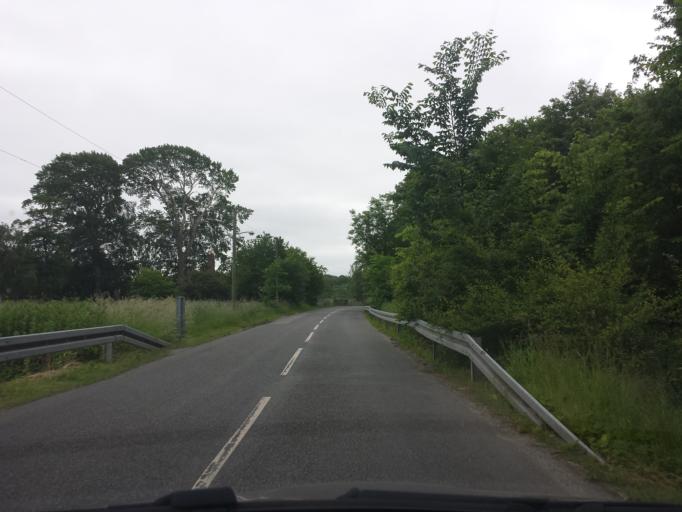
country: DK
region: Capital Region
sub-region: Ballerup Kommune
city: Ballerup
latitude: 55.7012
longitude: 12.3783
